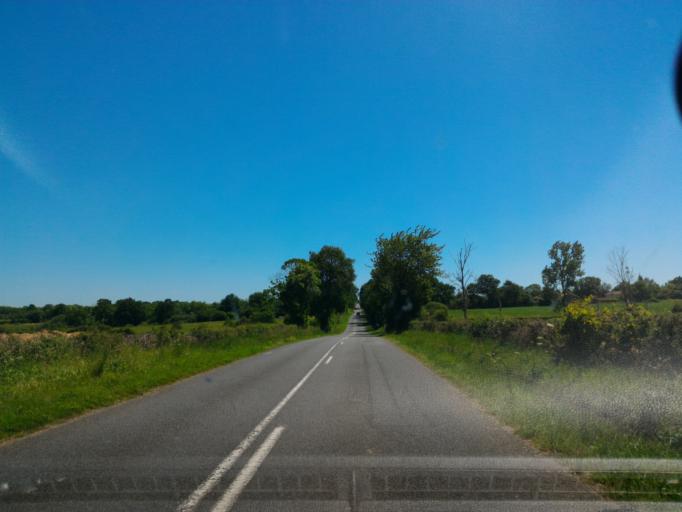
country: FR
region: Poitou-Charentes
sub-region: Departement de la Vienne
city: Availles-Limouzine
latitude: 46.1909
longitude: 0.7191
